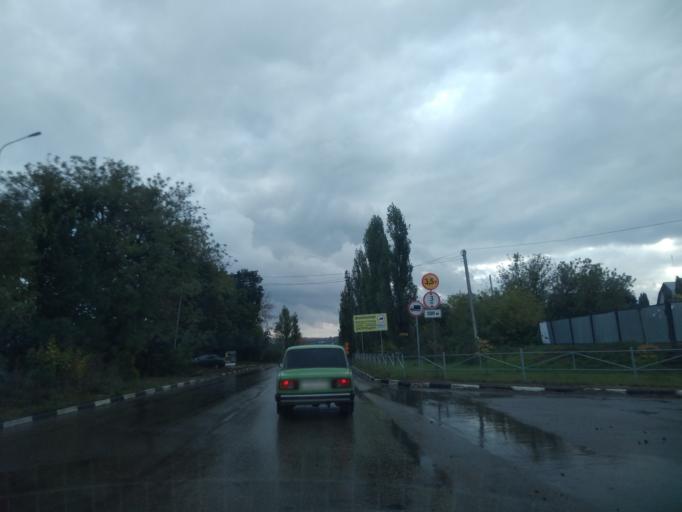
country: RU
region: Tula
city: Yefremov
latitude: 53.1327
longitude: 38.1179
